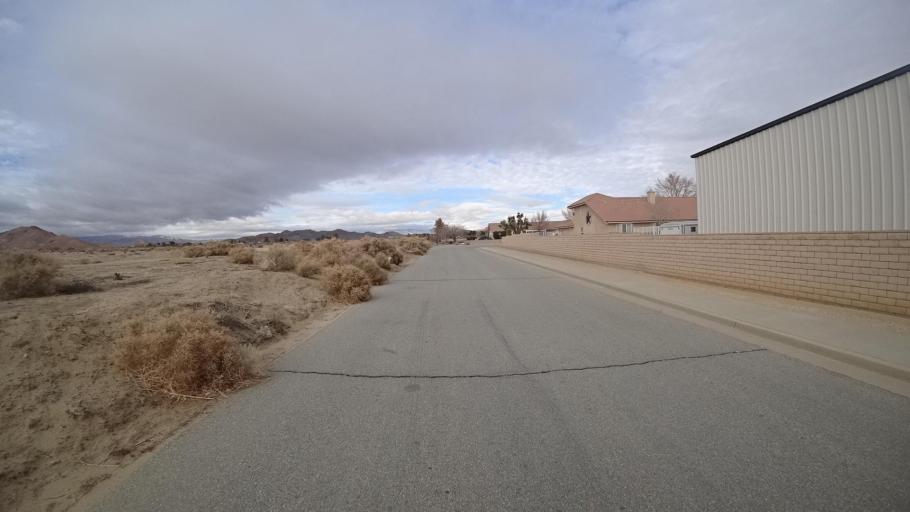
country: US
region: California
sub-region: Kern County
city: Rosamond
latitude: 34.8686
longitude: -118.2114
